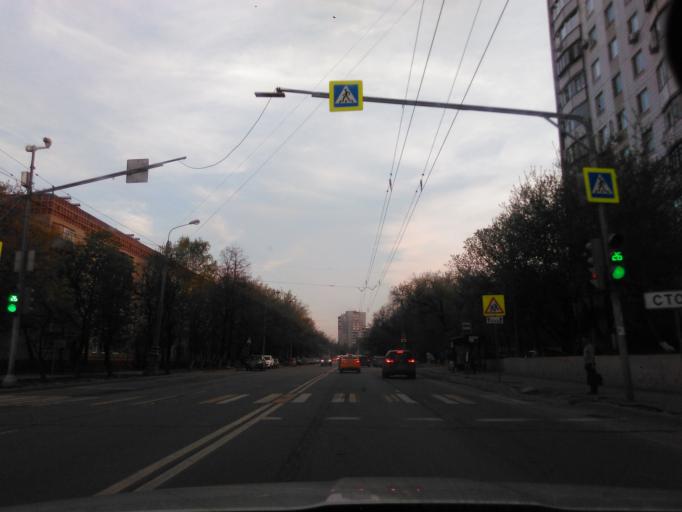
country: RU
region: Moscow
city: Lyublino
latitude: 55.6859
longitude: 37.7530
